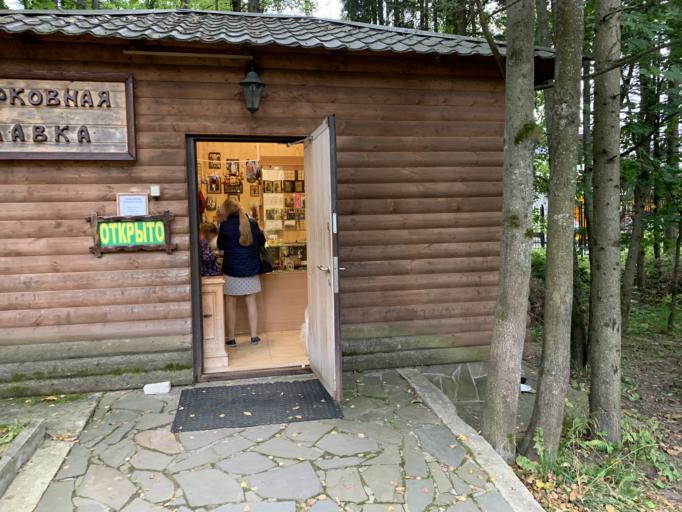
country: RU
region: Moskovskaya
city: Zvenigorod
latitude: 55.7354
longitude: 36.8114
